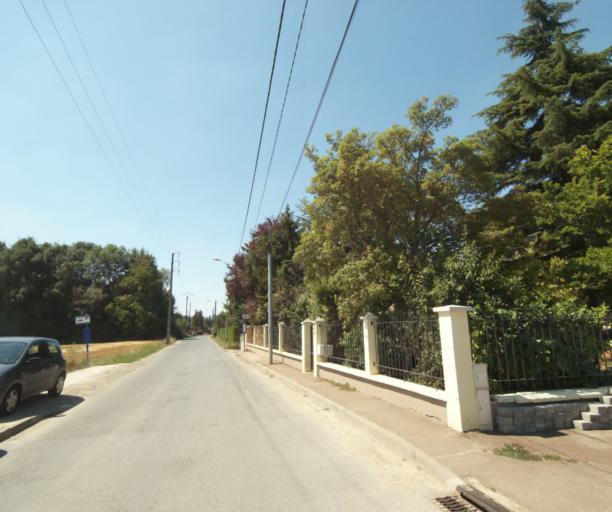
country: FR
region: Ile-de-France
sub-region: Departement de Seine-et-Marne
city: Dampmart
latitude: 48.8819
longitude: 2.7325
